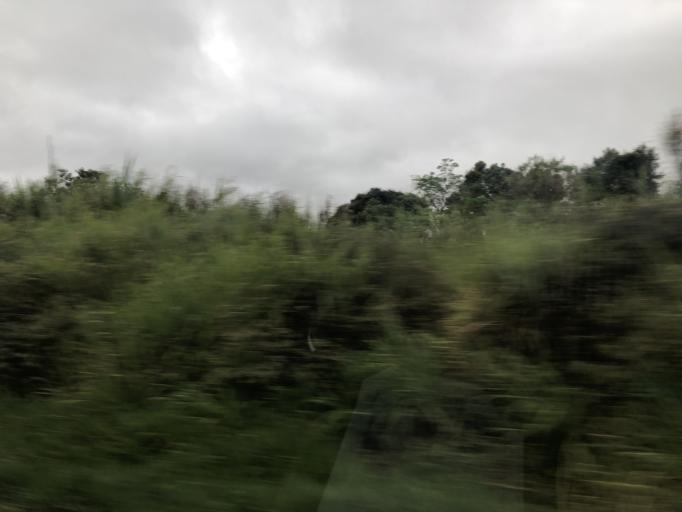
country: BR
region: Bahia
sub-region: Cruz Das Almas
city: Cruz das Almas
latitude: -12.6382
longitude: -39.0968
